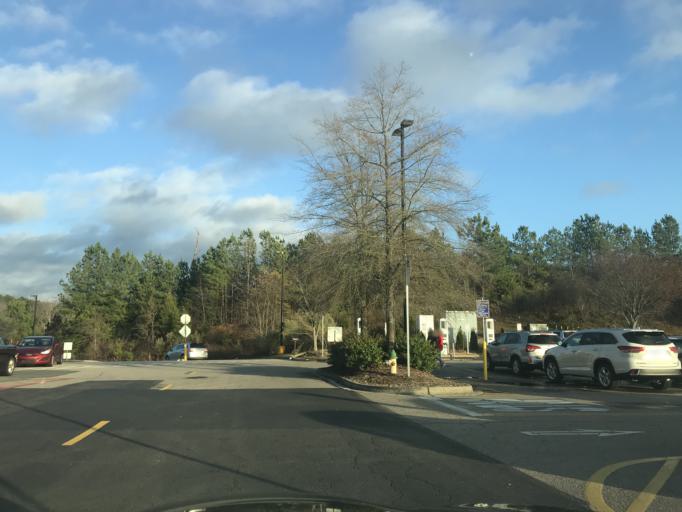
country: US
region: North Carolina
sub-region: Wake County
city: Wake Forest
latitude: 35.9518
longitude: -78.5344
